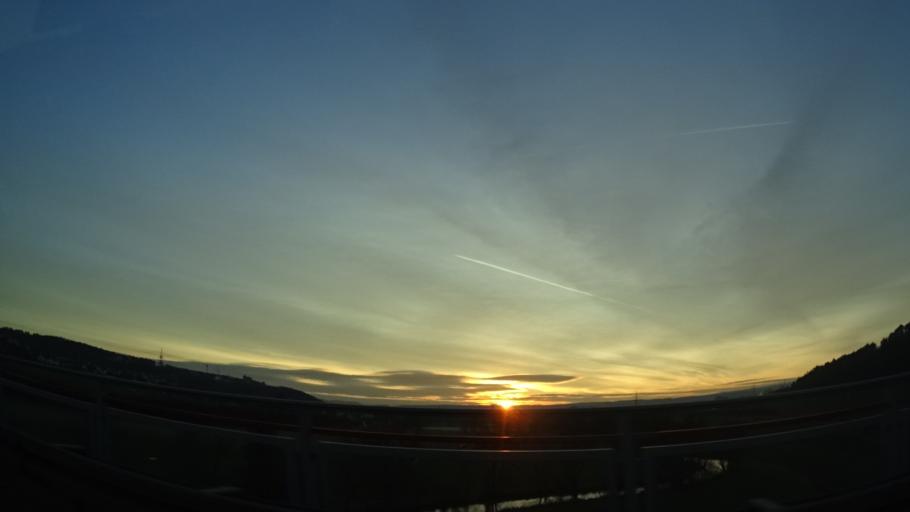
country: DE
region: Bavaria
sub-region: Regierungsbezirk Unterfranken
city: Heustreu
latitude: 50.3393
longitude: 10.2433
